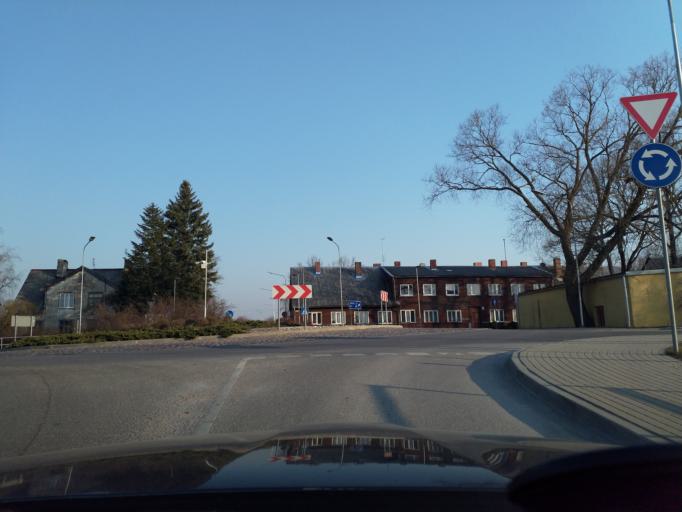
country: LV
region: Grobina
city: Grobina
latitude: 56.5345
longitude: 21.1896
